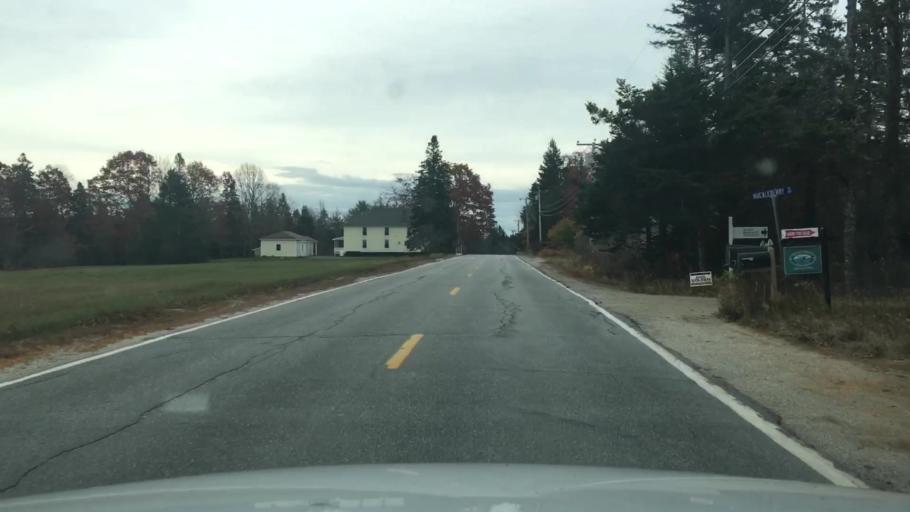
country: US
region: Maine
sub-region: Hancock County
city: Sedgwick
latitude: 44.3648
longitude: -68.5524
